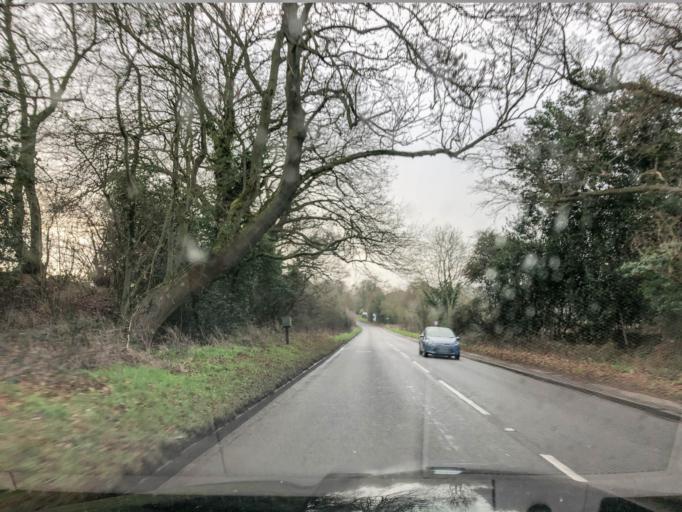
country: GB
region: England
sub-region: Warwickshire
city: Kenilworth
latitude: 52.3268
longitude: -1.5751
